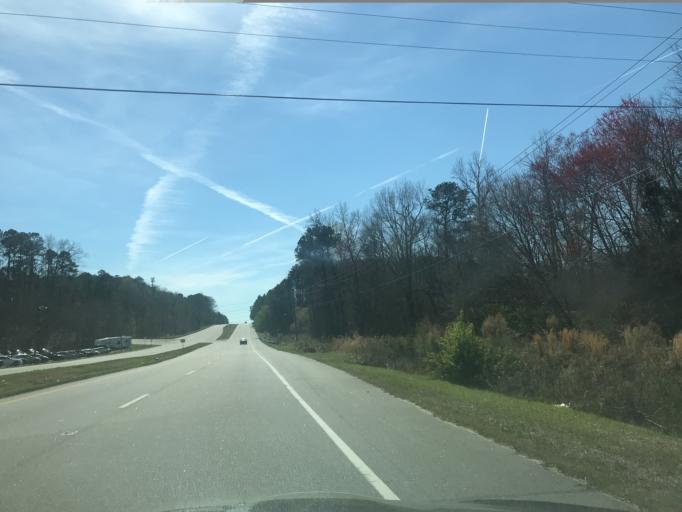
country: US
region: North Carolina
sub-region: Wake County
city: Fuquay-Varina
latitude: 35.6159
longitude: -78.7357
